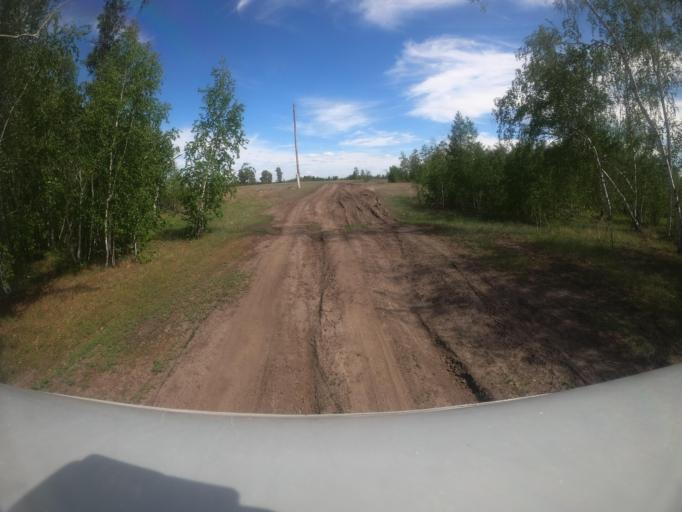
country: RU
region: Sakha
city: Markha
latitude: 62.2253
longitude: 129.7118
